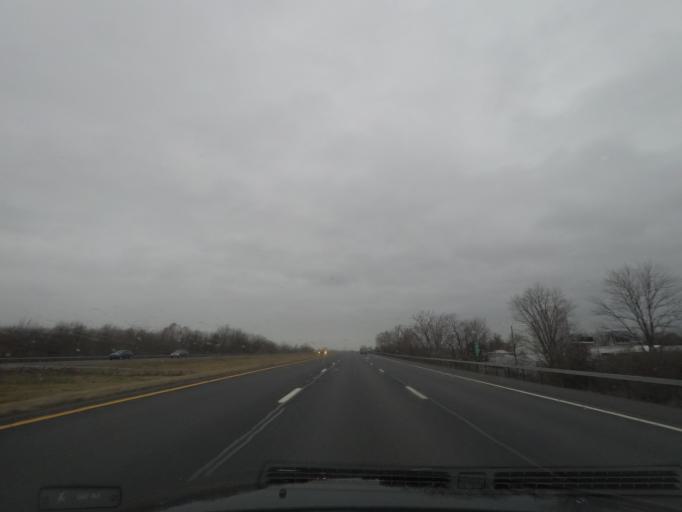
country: US
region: New York
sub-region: Rensselaer County
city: Hampton Manor
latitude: 42.6404
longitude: -73.7092
